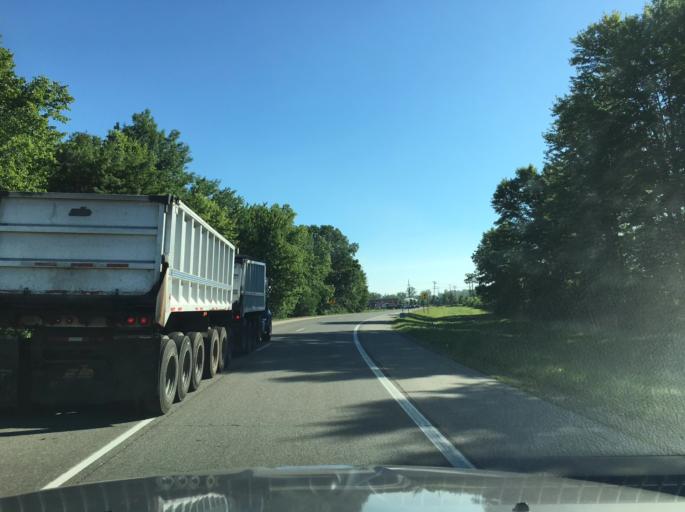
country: US
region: Michigan
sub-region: Macomb County
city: Shelby
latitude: 42.6670
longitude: -83.0140
